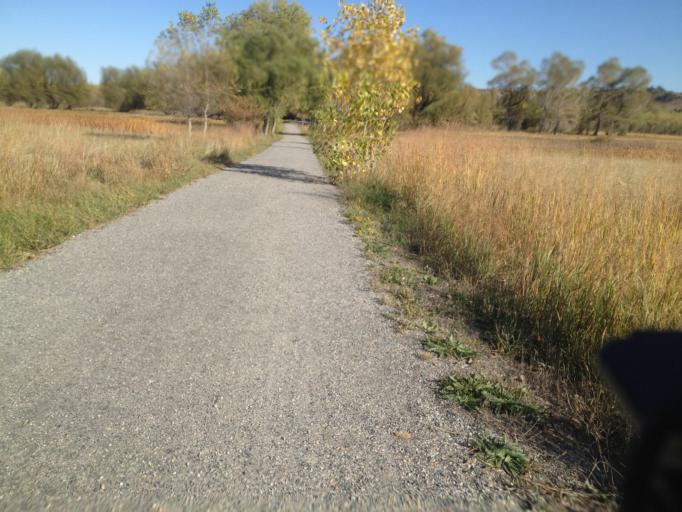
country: US
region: Colorado
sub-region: Boulder County
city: Boulder
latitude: 39.9679
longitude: -105.2353
